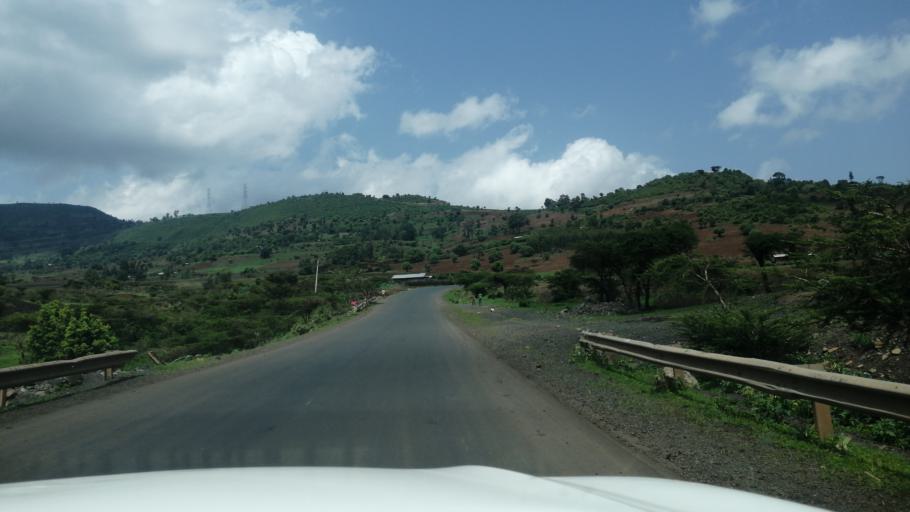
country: ET
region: Oromiya
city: Gedo
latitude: 8.9799
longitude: 37.6030
